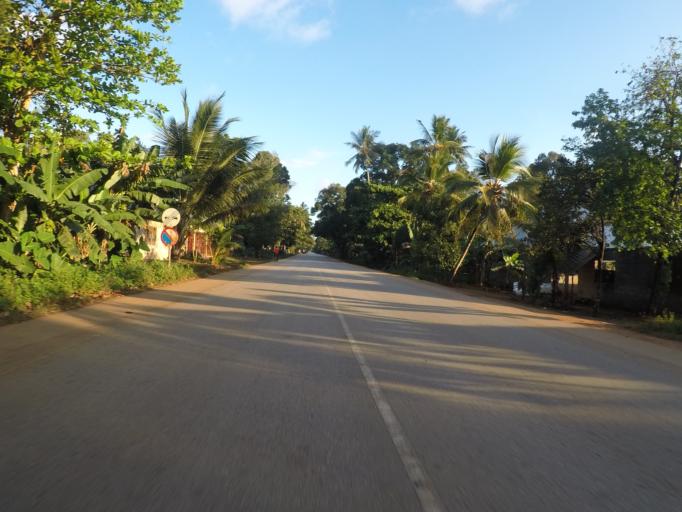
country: TZ
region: Zanzibar North
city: Mkokotoni
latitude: -5.8701
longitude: 39.2808
